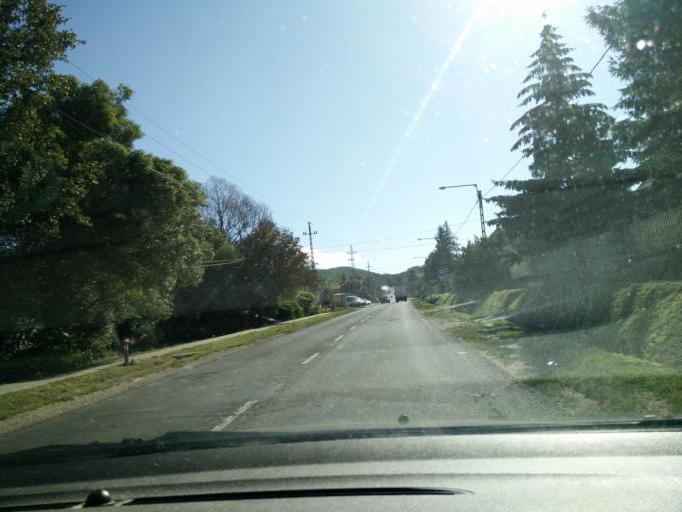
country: HU
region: Pest
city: Piliscsaba
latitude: 47.6318
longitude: 18.8362
